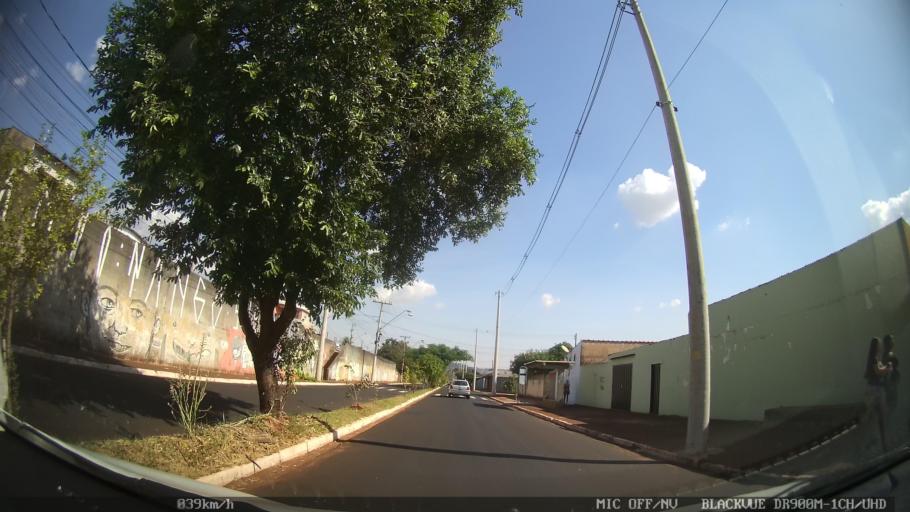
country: BR
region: Sao Paulo
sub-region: Ribeirao Preto
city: Ribeirao Preto
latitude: -21.1931
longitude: -47.8472
